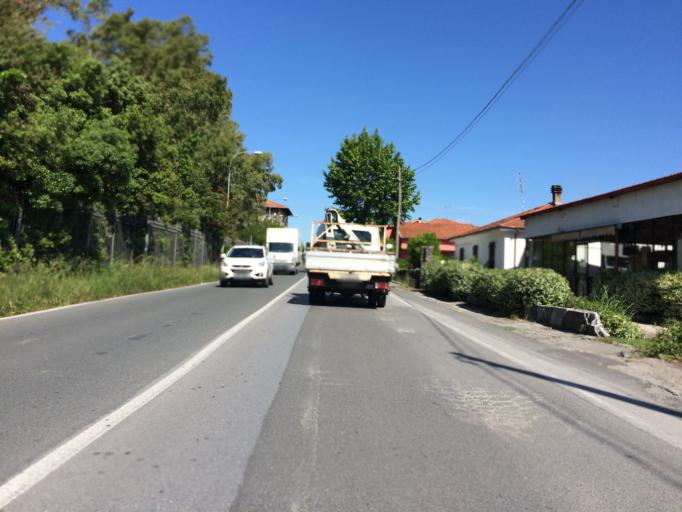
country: IT
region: Tuscany
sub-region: Provincia di Massa-Carrara
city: Borghetto-Melara
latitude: 44.1004
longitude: 9.9821
